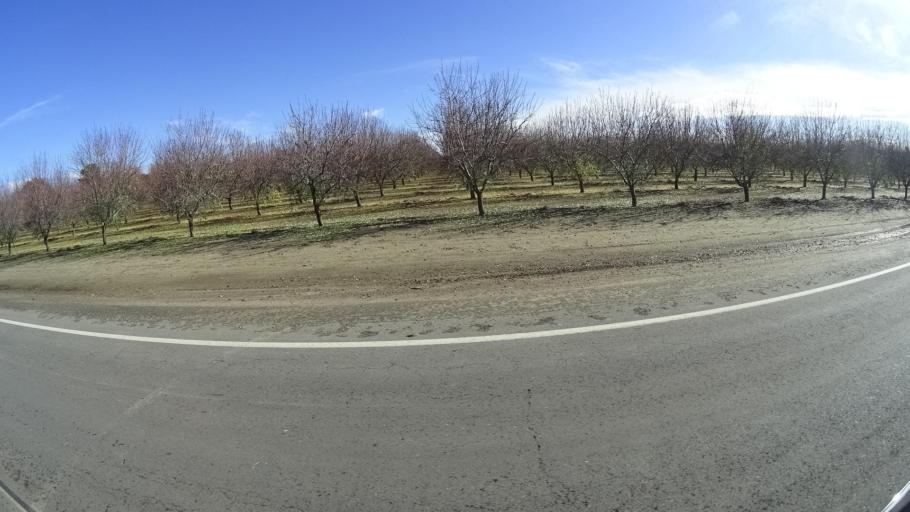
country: US
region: California
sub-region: Kern County
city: Rosedale
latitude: 35.3640
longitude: -119.1988
